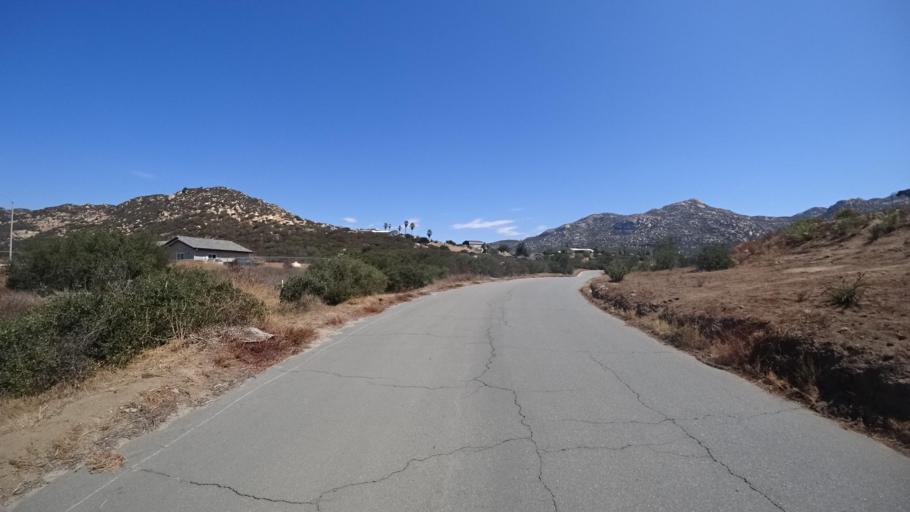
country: US
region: California
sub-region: San Diego County
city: San Diego Country Estates
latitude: 32.9501
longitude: -116.8358
